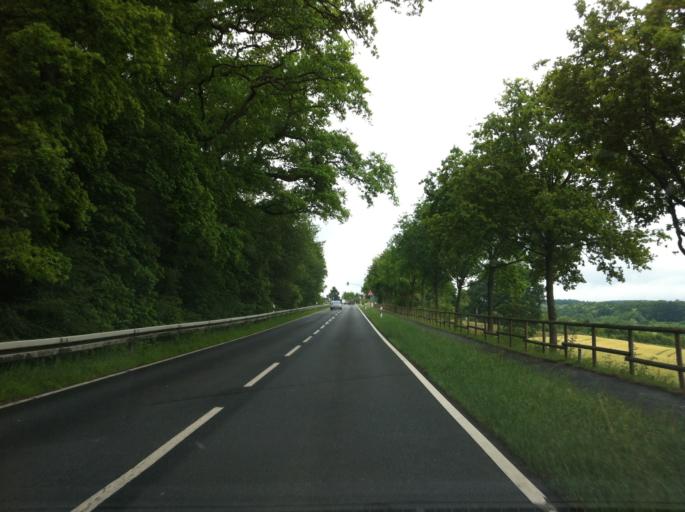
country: DE
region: Hesse
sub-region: Regierungsbezirk Darmstadt
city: Bad Soden am Taunus
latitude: 50.1551
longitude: 8.5076
